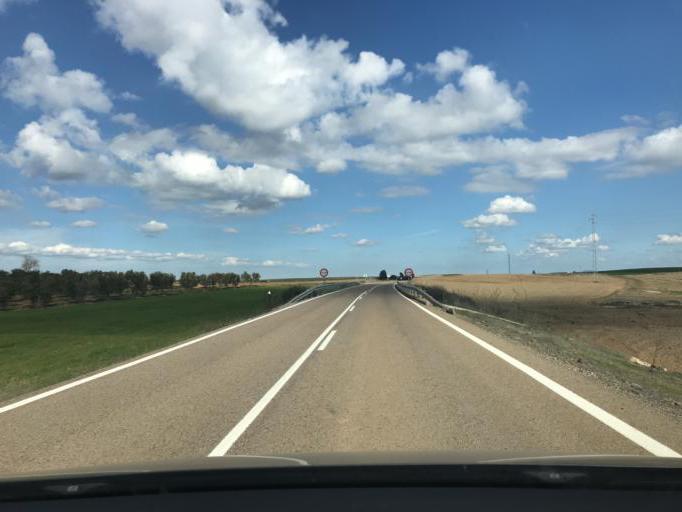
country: ES
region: Extremadura
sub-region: Provincia de Badajoz
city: Valverde de Llerena
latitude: 38.2483
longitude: -5.7616
